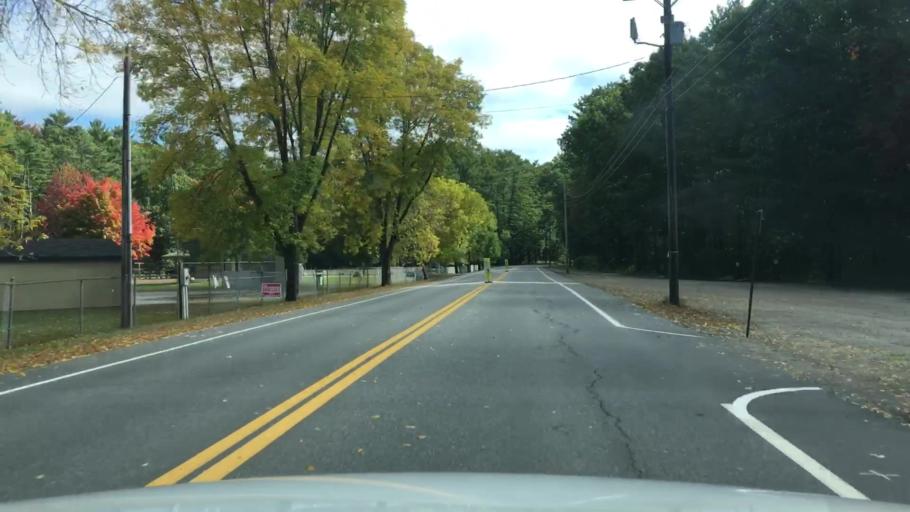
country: US
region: Maine
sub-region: Cumberland County
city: Brunswick
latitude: 43.9233
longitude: -69.9405
